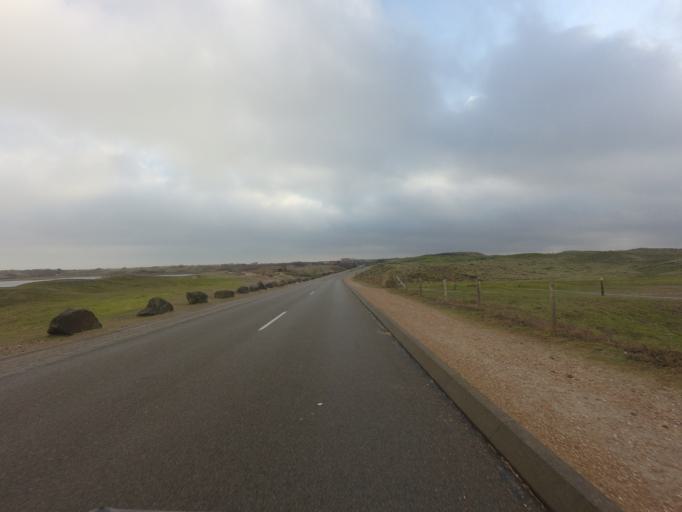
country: NL
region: North Holland
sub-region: Gemeente Texel
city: Den Burg
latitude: 53.1801
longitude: 4.8573
